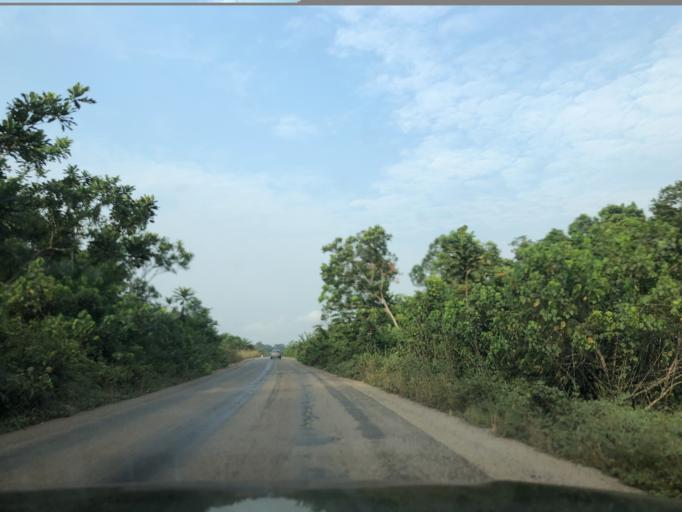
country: CM
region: Littoral
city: Dizangue
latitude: 3.3860
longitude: 10.1077
